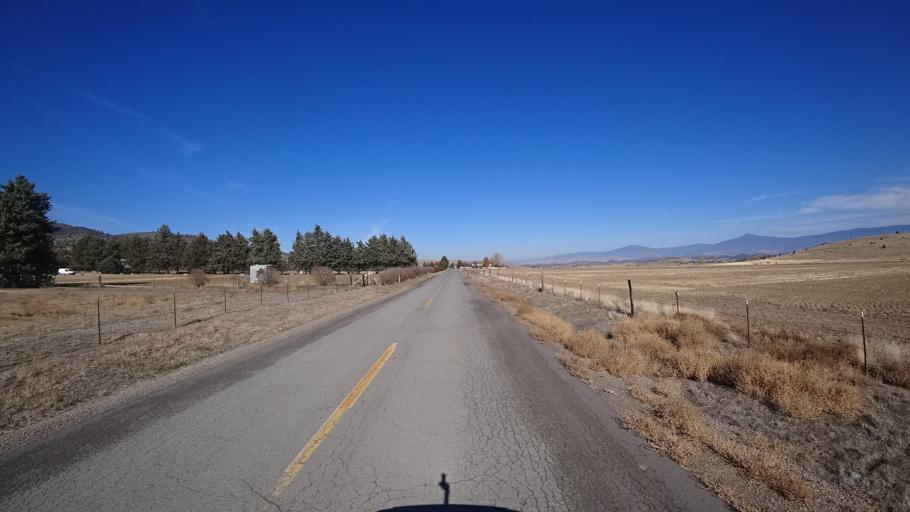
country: US
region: California
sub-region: Siskiyou County
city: Montague
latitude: 41.5810
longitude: -122.5456
